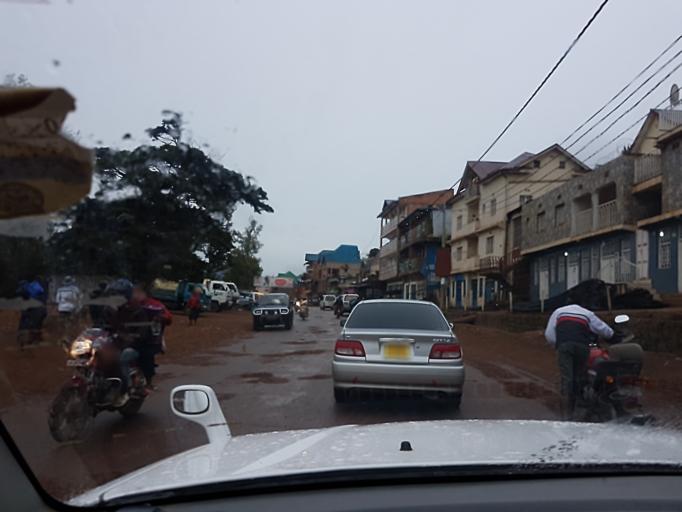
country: CD
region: South Kivu
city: Bukavu
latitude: -2.4967
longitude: 28.8503
